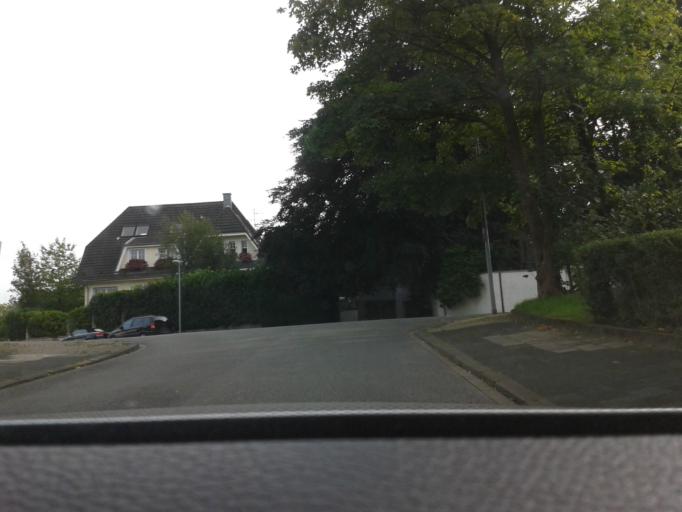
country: DE
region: North Rhine-Westphalia
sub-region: Regierungsbezirk Dusseldorf
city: Duisburg
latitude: 51.4305
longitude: 6.8202
